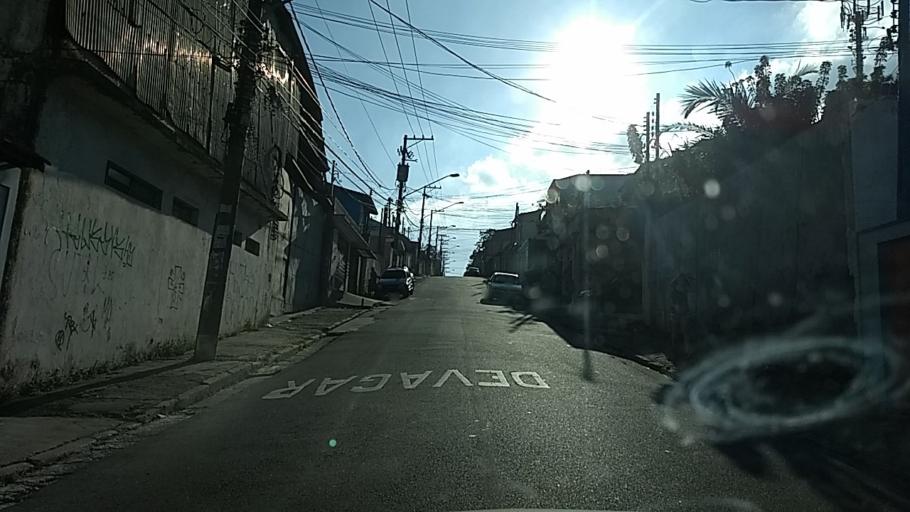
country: BR
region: Sao Paulo
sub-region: Guarulhos
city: Guarulhos
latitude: -23.4836
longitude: -46.5957
